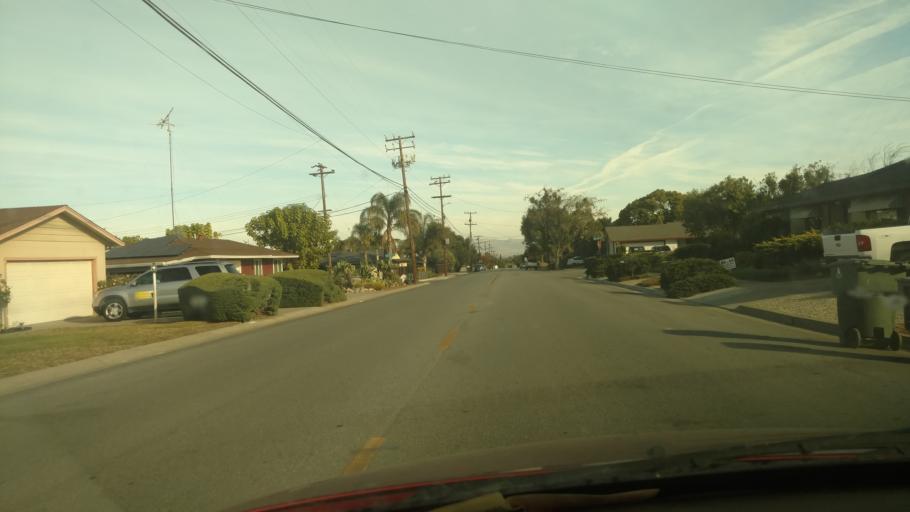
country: US
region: California
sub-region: San Benito County
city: Ridgemark
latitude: 36.8332
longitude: -121.3814
